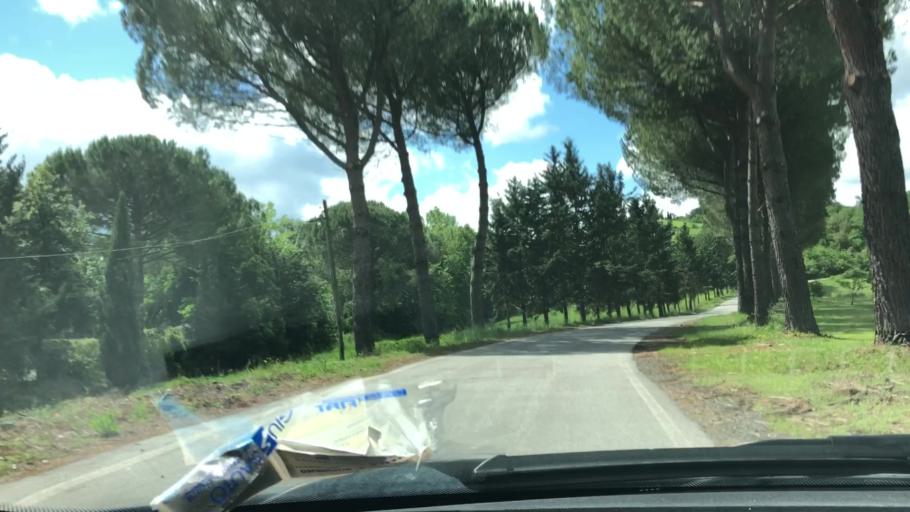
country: IT
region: Tuscany
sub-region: Province of Pisa
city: Saline
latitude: 43.3493
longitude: 10.7928
